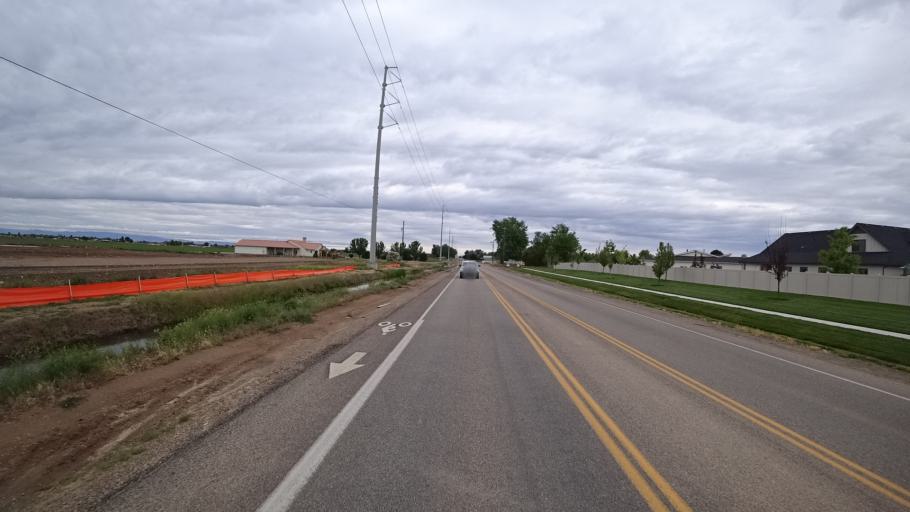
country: US
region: Idaho
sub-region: Ada County
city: Meridian
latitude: 43.6485
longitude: -116.4425
